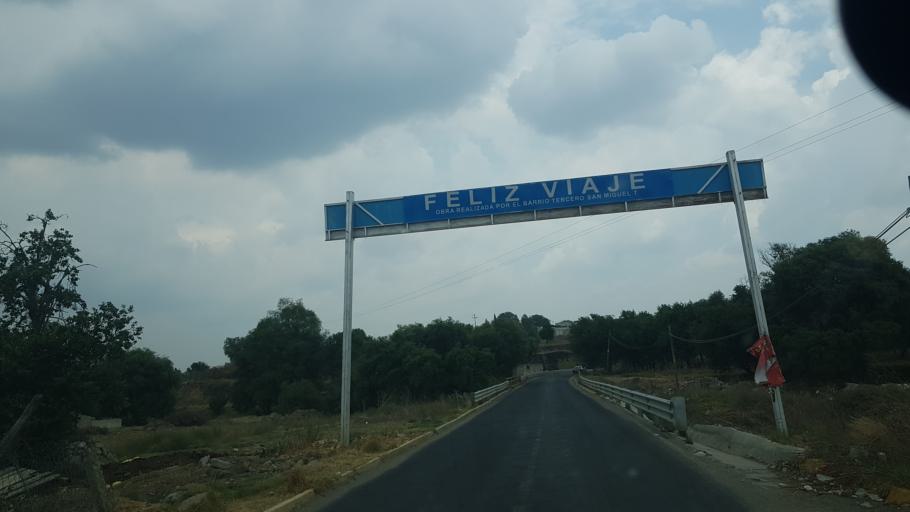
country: MX
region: Puebla
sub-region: Huejotzingo
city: San Miguel Tianguizolco
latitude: 19.1600
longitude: -98.4337
